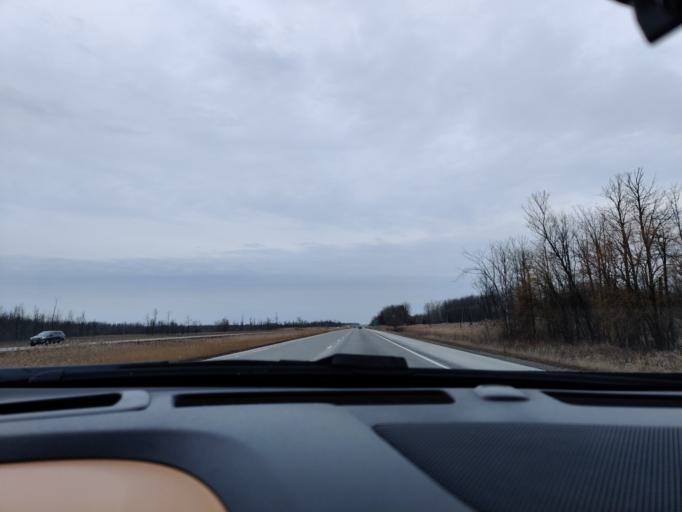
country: US
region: New York
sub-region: St. Lawrence County
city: Norfolk
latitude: 44.9248
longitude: -75.1793
